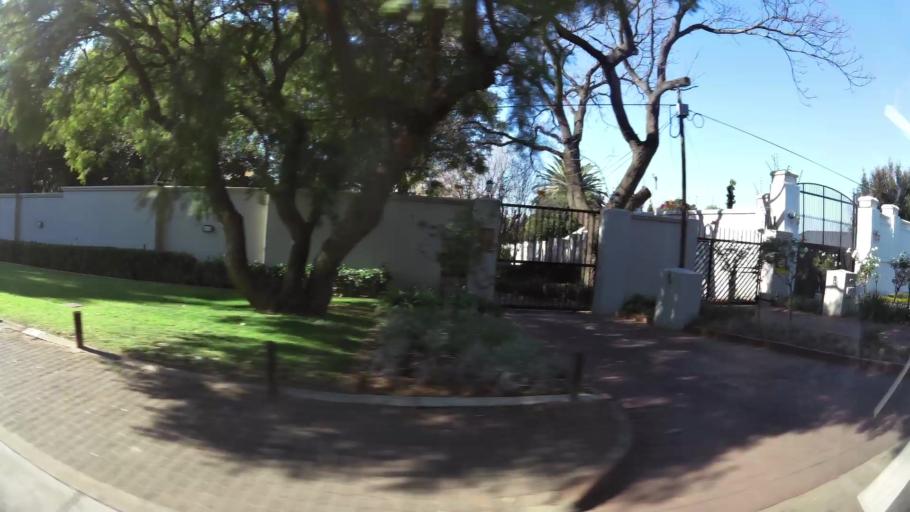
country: ZA
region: Gauteng
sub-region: City of Johannesburg Metropolitan Municipality
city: Midrand
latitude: -26.0619
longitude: 28.0280
